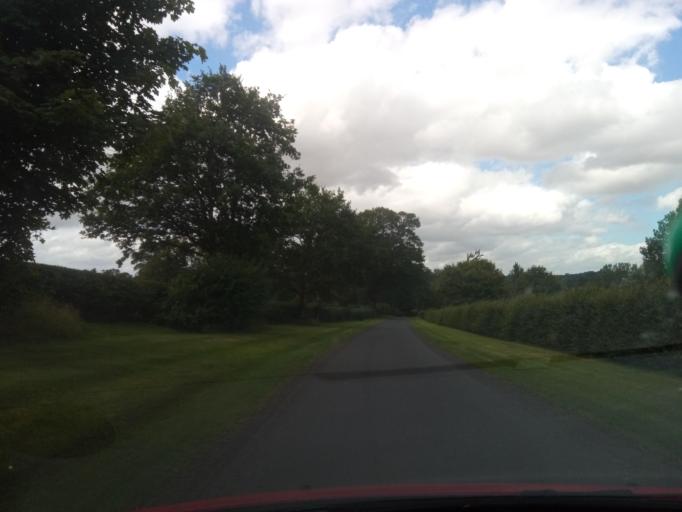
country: GB
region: Scotland
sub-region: The Scottish Borders
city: Coldstream
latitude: 55.6525
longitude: -2.2731
